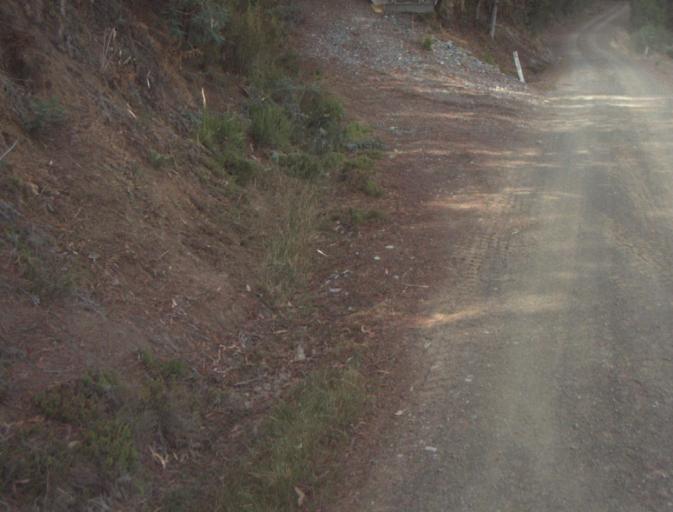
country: AU
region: Tasmania
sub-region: Launceston
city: Mayfield
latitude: -41.2974
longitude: 147.2145
